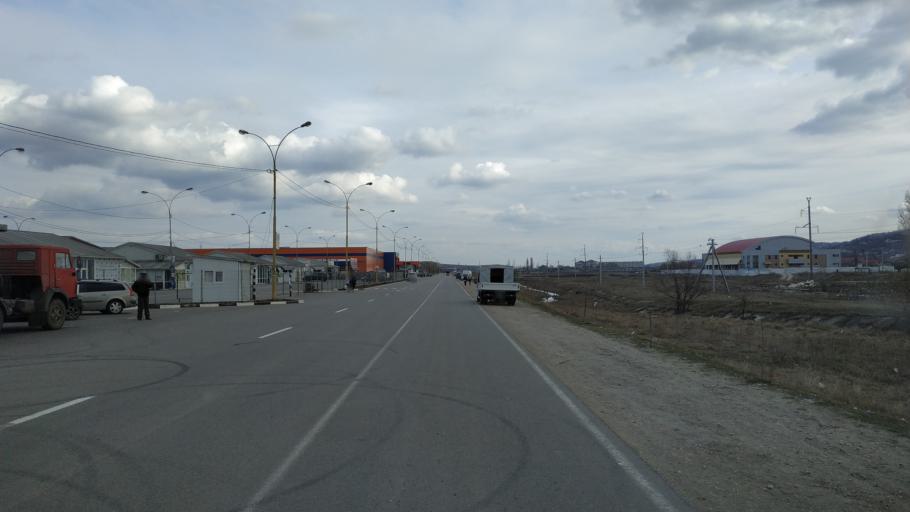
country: MD
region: Hincesti
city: Hincesti
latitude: 46.8319
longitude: 28.5978
